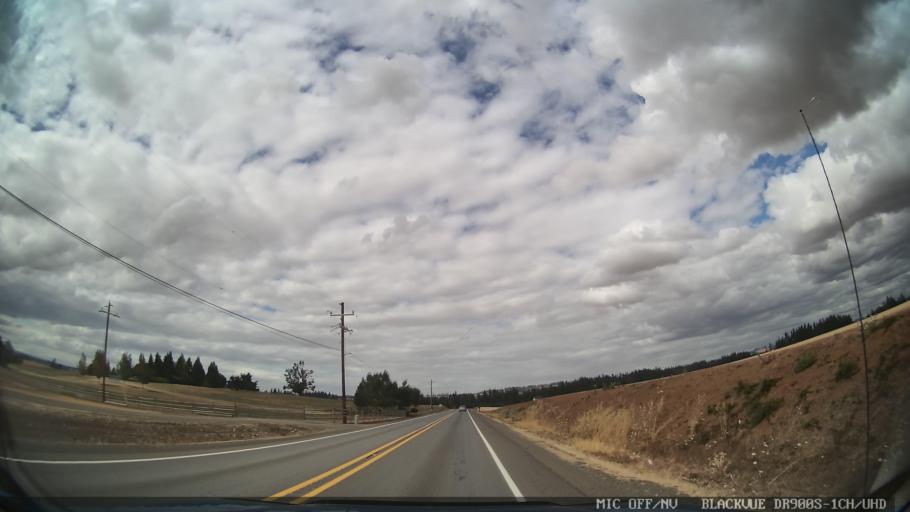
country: US
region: Oregon
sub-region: Marion County
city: Sublimity
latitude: 44.8409
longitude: -122.7946
